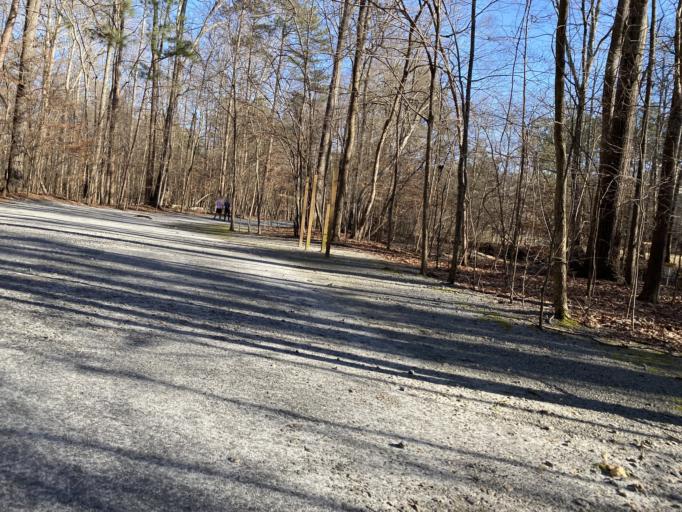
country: US
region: Georgia
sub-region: Cobb County
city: Kennesaw
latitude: 34.0534
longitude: -84.6315
